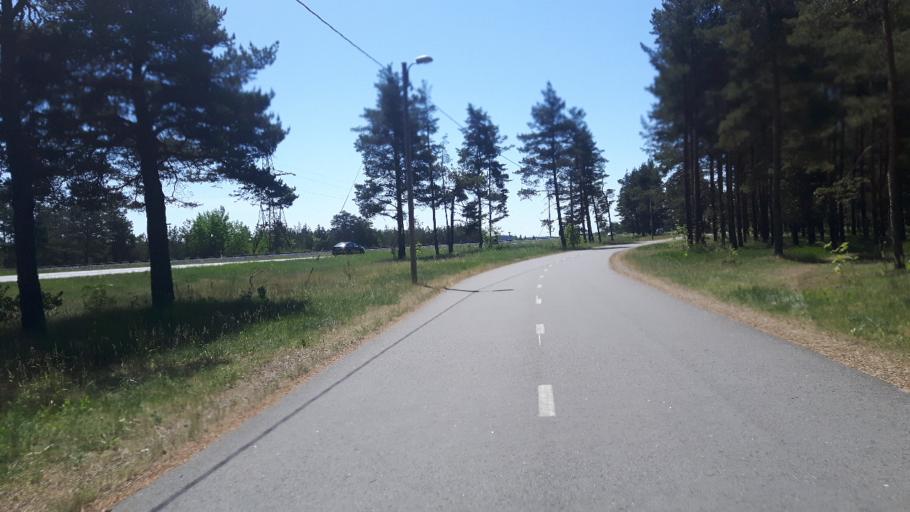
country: EE
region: Harju
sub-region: Tallinna linn
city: Tallinn
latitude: 59.3625
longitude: 24.7165
